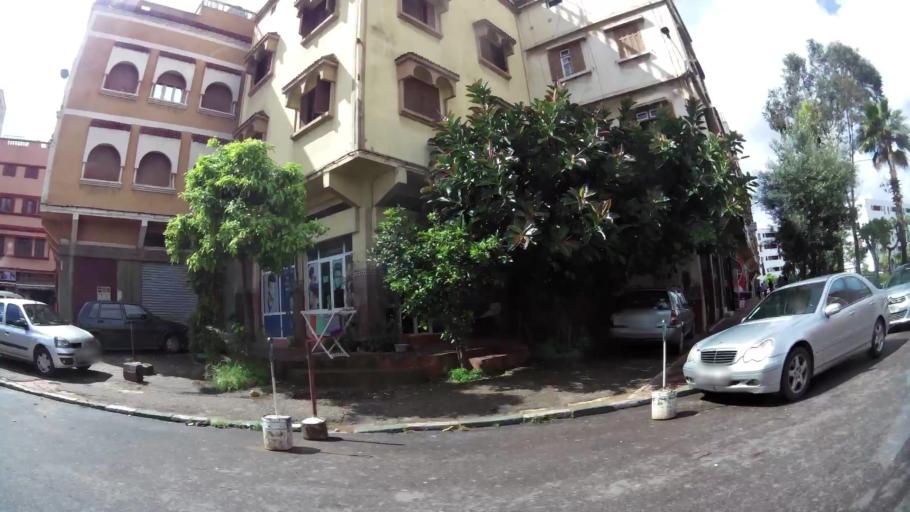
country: MA
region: Grand Casablanca
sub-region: Casablanca
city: Casablanca
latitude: 33.5496
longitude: -7.6004
